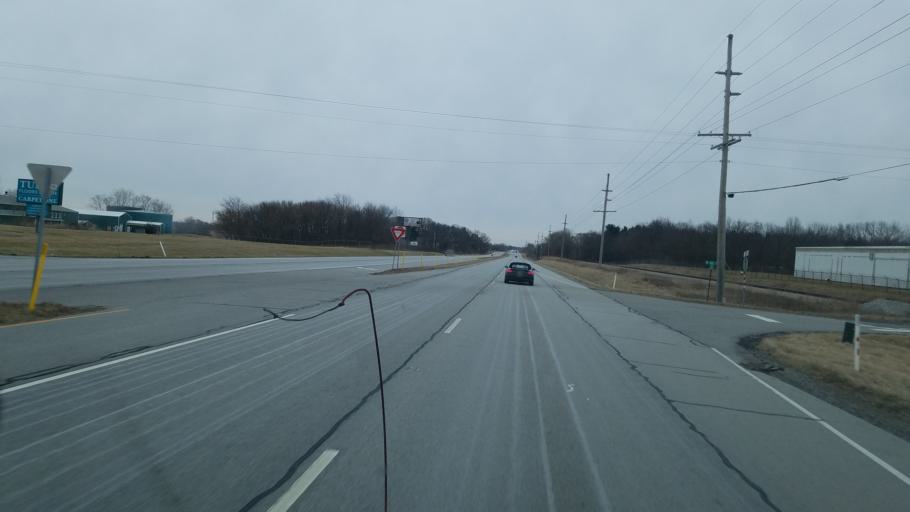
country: US
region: Indiana
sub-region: Porter County
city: Valparaiso
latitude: 41.4433
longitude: -86.9888
